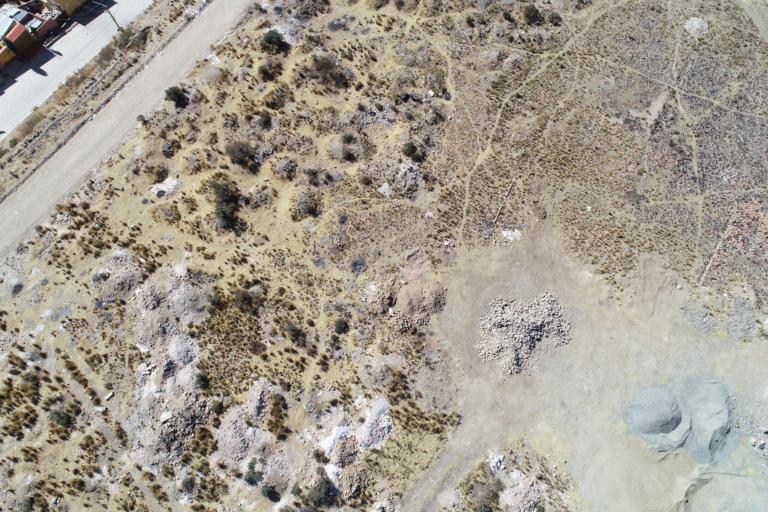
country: BO
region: La Paz
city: La Paz
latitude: -16.5408
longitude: -68.1531
